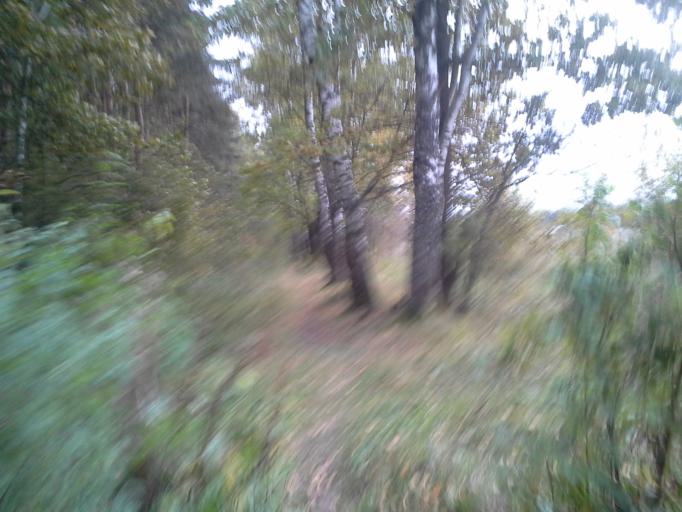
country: RU
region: Moskovskaya
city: Kokoshkino
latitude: 55.6078
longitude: 37.1566
